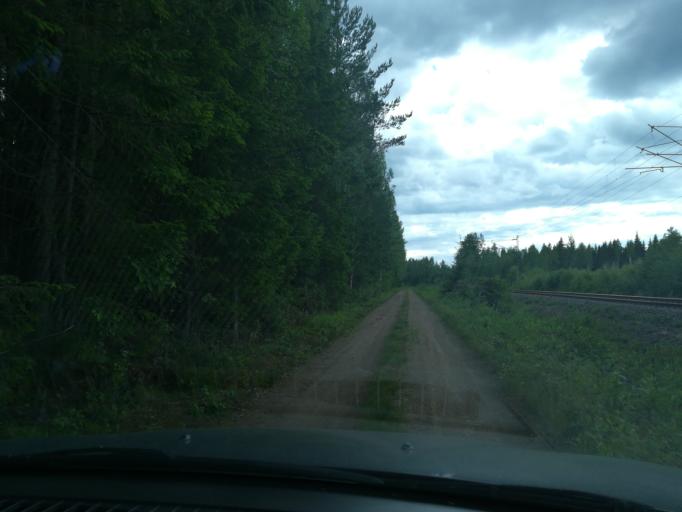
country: FI
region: Southern Savonia
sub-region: Mikkeli
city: Mikkeli
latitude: 61.6742
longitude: 27.1123
